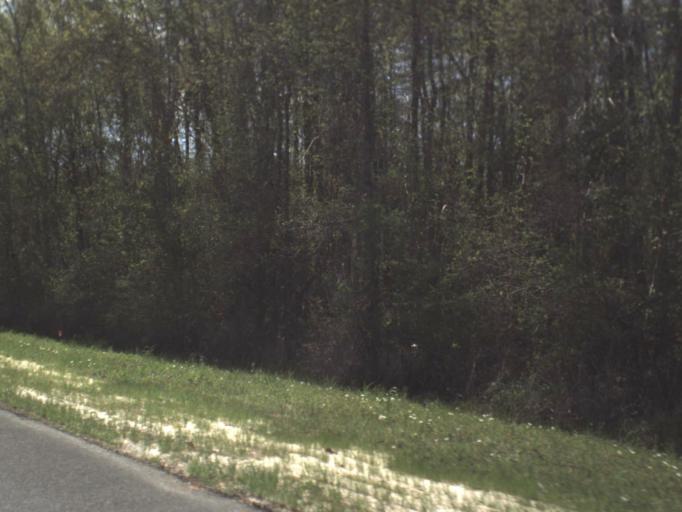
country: US
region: Alabama
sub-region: Geneva County
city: Geneva
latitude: 30.8773
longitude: -85.9484
